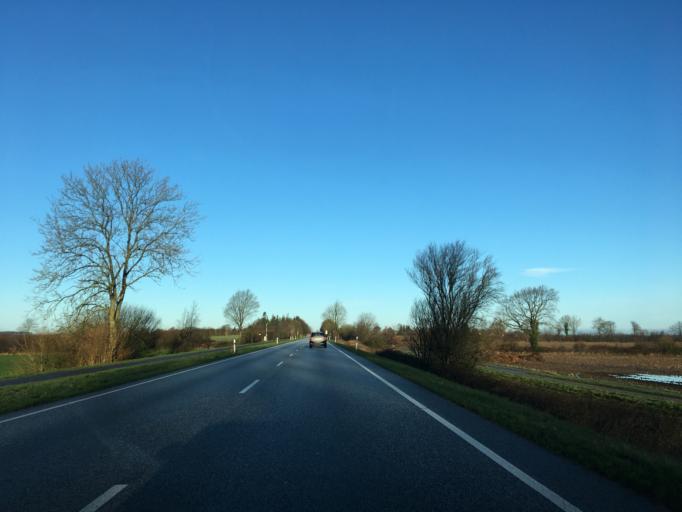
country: DE
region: Schleswig-Holstein
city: Neudorf-Bornstein
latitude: 54.4276
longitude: 9.9552
